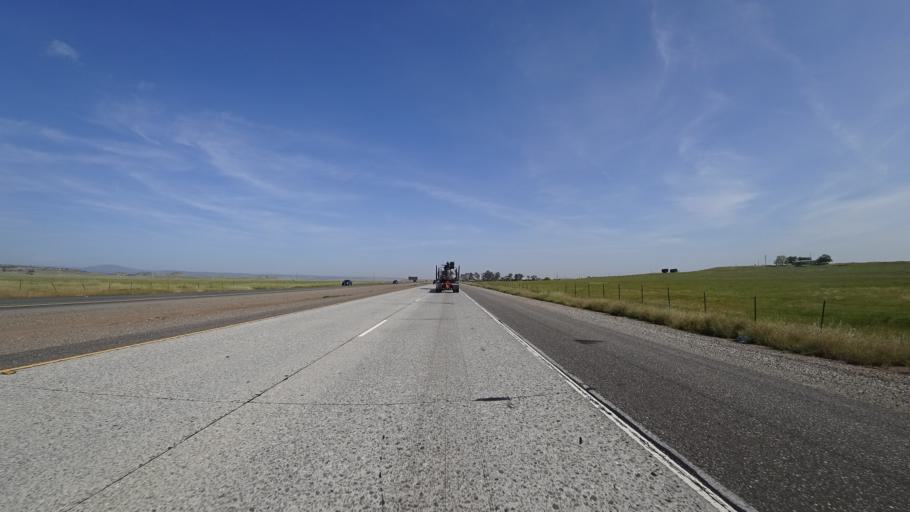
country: US
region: California
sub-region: Butte County
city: Durham
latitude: 39.6559
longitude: -121.7319
